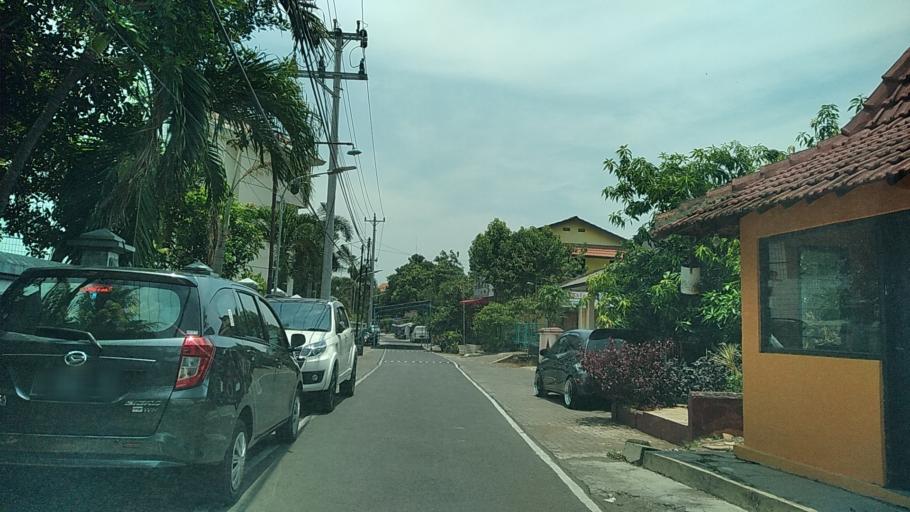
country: ID
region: Central Java
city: Semarang
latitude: -7.0594
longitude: 110.4118
